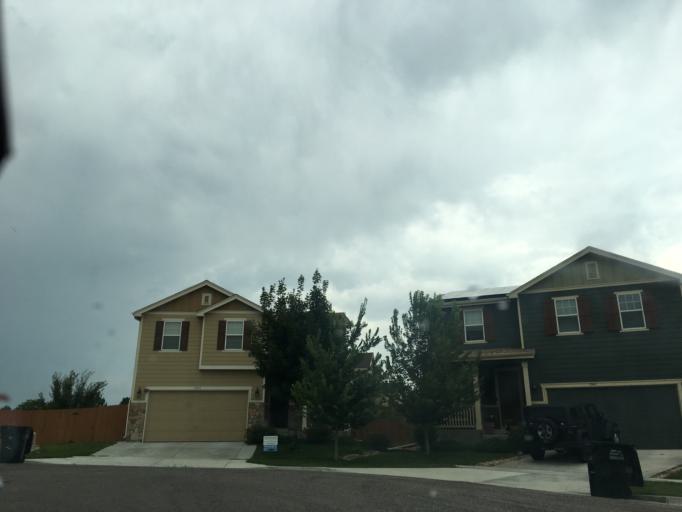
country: US
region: Colorado
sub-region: Arapahoe County
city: Sheridan
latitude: 39.6556
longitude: -105.0339
